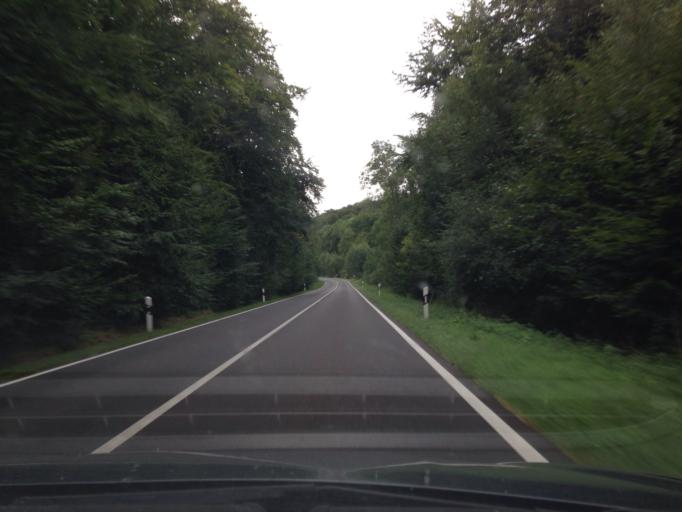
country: DE
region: Mecklenburg-Vorpommern
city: Loitz
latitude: 53.3463
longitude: 13.4135
